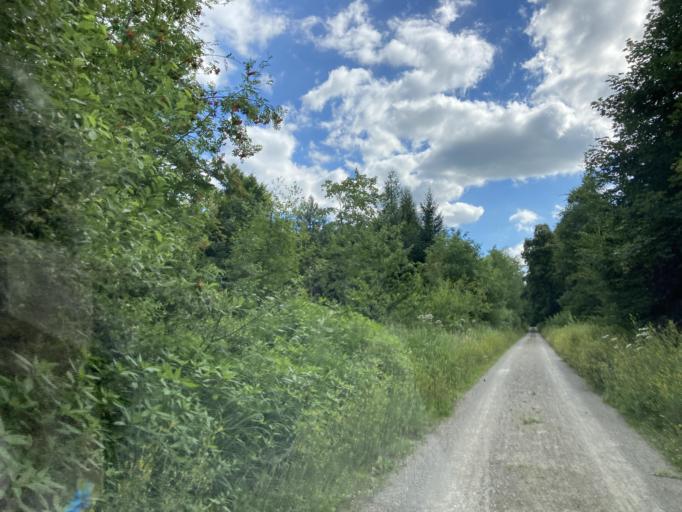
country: DE
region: Baden-Wuerttemberg
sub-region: Tuebingen Region
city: Ofterdingen
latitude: 48.4405
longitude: 9.0106
